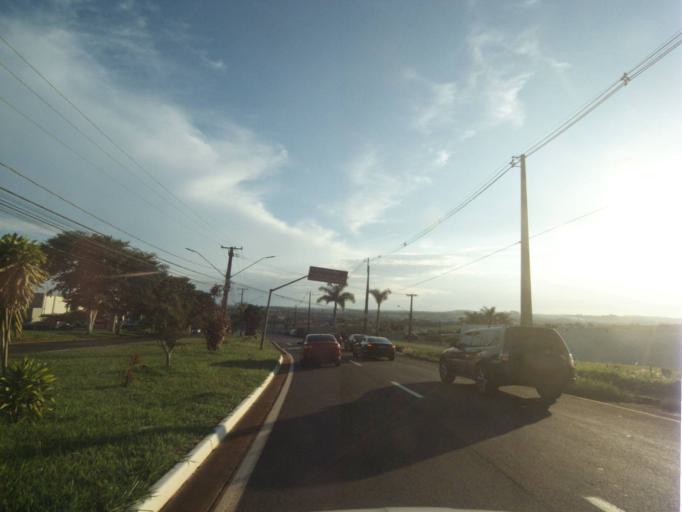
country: BR
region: Parana
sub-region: Londrina
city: Londrina
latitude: -23.3452
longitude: -51.1893
